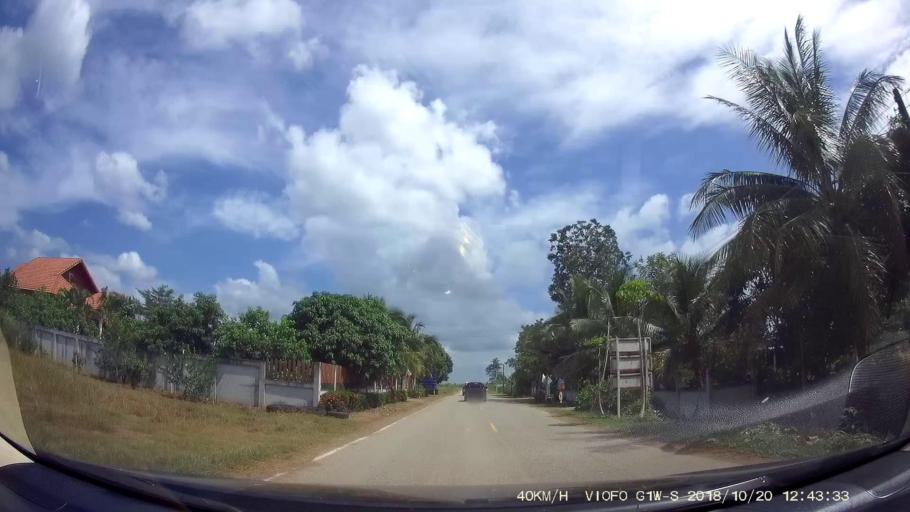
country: TH
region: Chaiyaphum
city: Khon San
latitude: 16.5414
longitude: 101.8619
